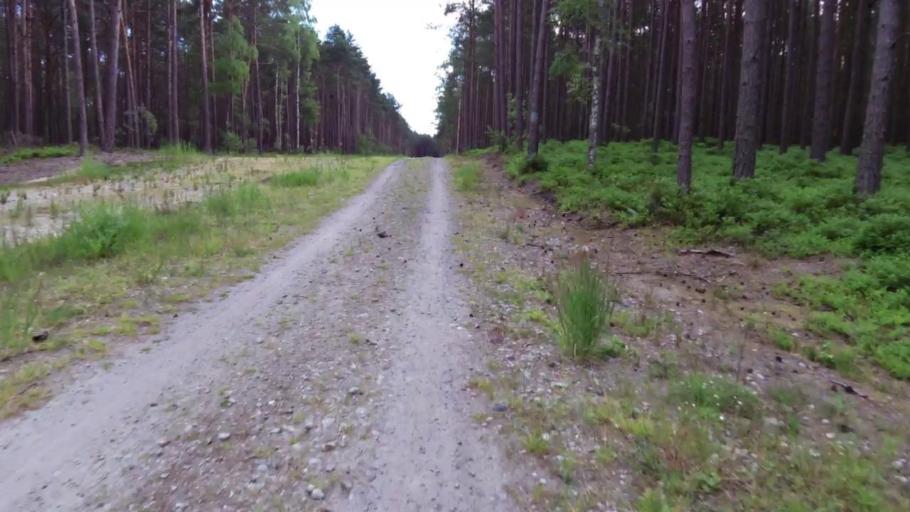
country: PL
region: West Pomeranian Voivodeship
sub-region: Powiat kamienski
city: Miedzyzdroje
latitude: 53.9029
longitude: 14.3577
